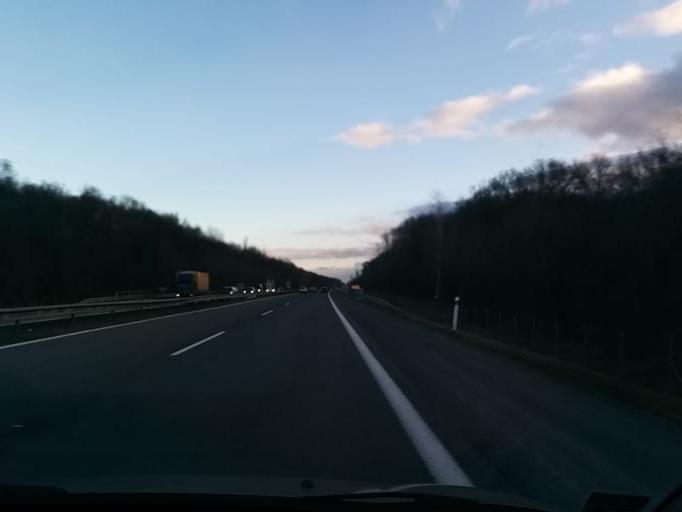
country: SK
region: Trnavsky
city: Leopoldov
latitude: 48.4713
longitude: 17.7431
